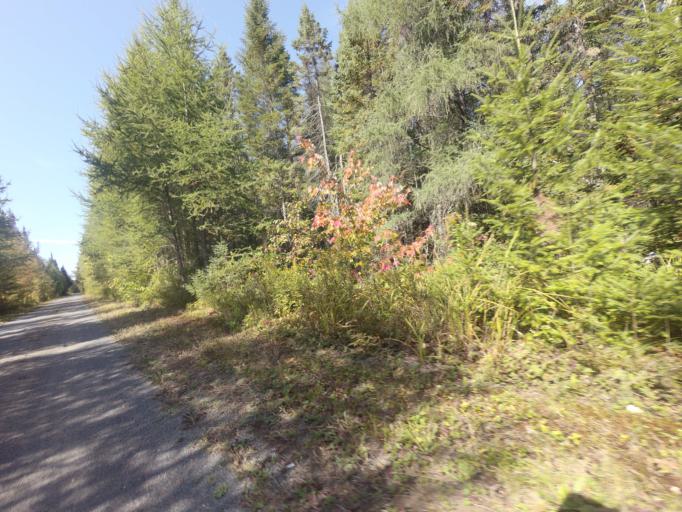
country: CA
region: Quebec
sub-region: Laurentides
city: Sainte-Agathe-des-Monts
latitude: 46.1038
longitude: -74.3786
